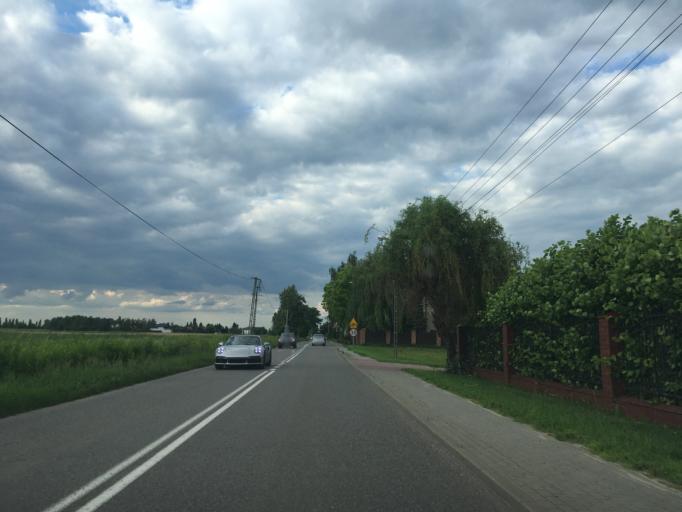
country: PL
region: Masovian Voivodeship
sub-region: Powiat piaseczynski
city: Lesznowola
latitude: 52.0969
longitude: 20.9739
